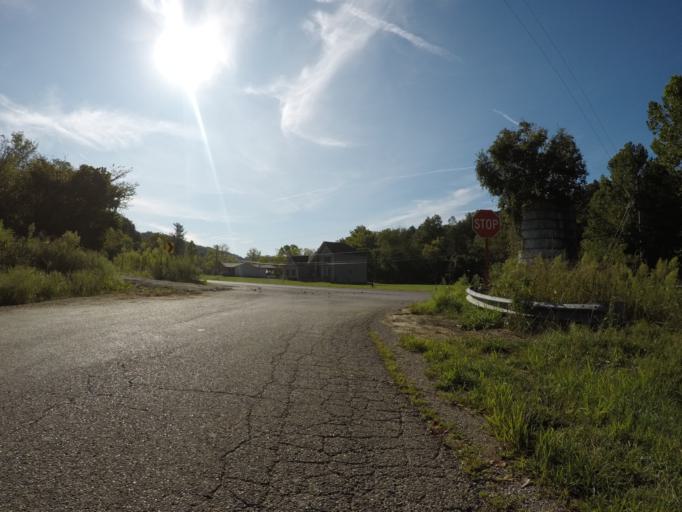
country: US
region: Ohio
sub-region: Lawrence County
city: Burlington
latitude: 38.4991
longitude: -82.5101
